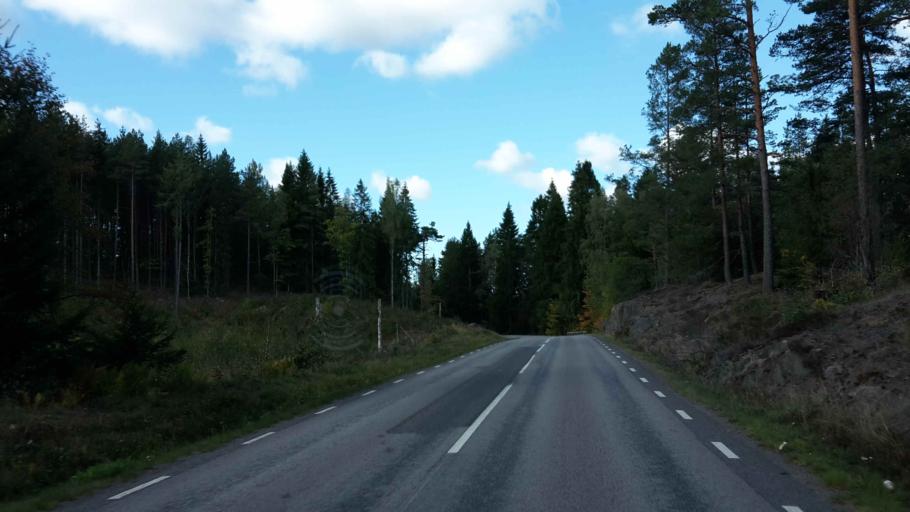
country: SE
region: OEstergoetland
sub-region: Atvidabergs Kommun
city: Atvidaberg
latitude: 58.1728
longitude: 16.1336
